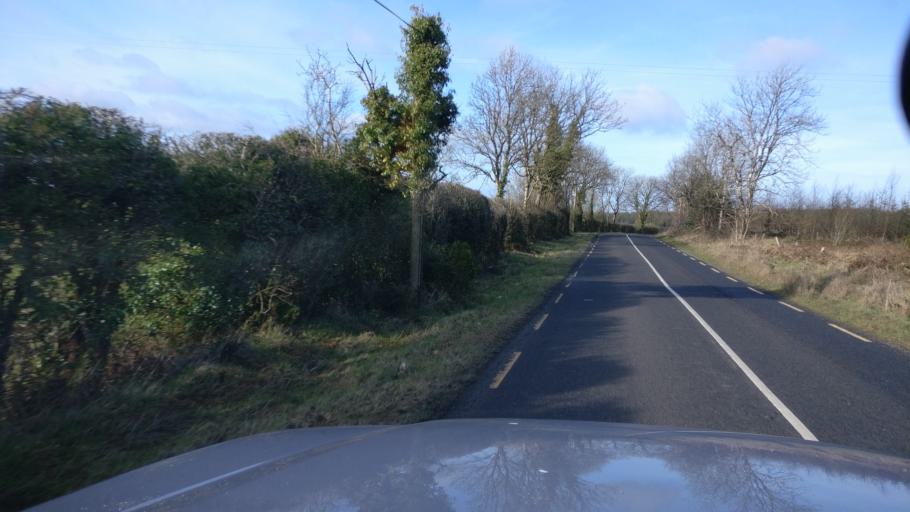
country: IE
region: Leinster
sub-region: Laois
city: Stradbally
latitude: 52.9166
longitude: -7.1870
